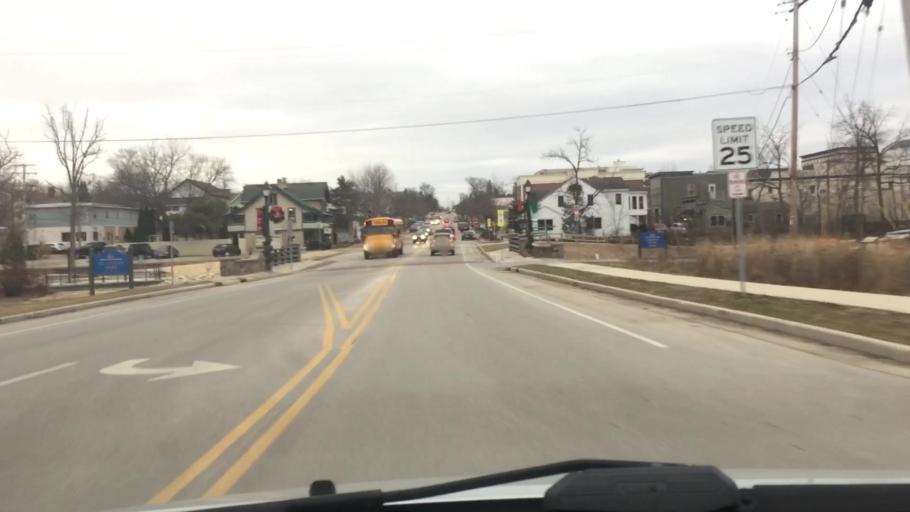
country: US
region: Wisconsin
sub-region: Waukesha County
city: Delafield
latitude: 43.0633
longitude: -88.4041
